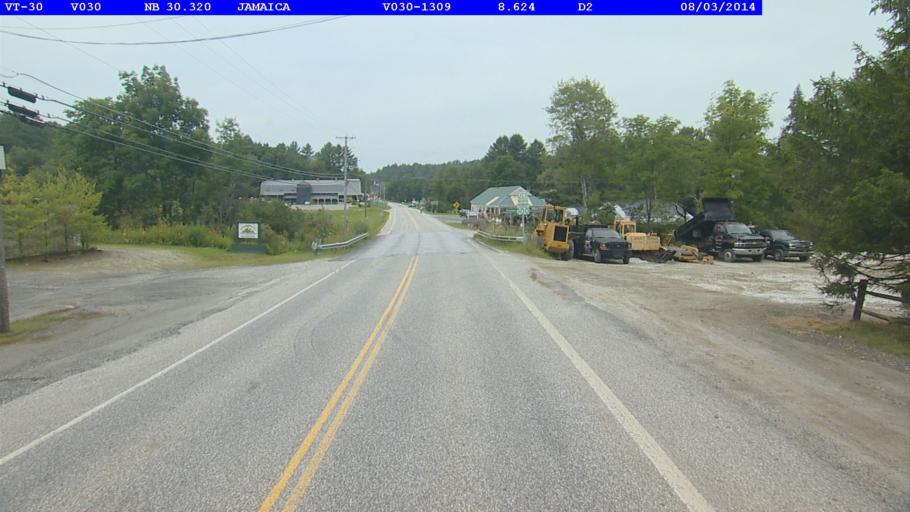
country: US
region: Vermont
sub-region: Windham County
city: Dover
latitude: 43.1461
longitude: -72.8372
